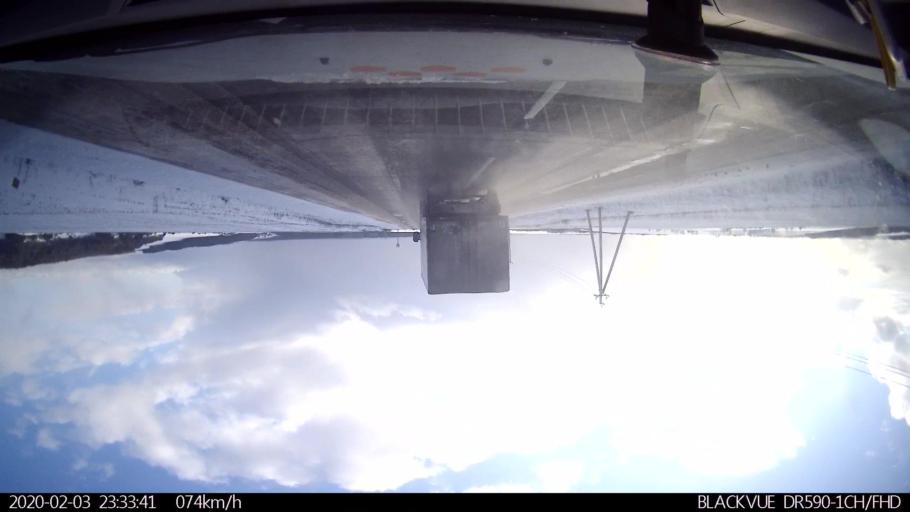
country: RU
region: Nizjnij Novgorod
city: Dal'neye Konstantinovo
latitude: 55.9285
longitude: 44.2177
